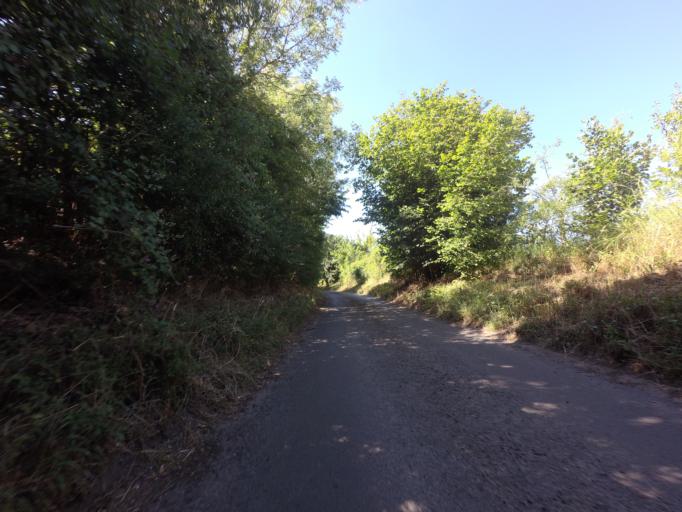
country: GB
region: England
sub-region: Kent
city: Dartford
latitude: 51.4069
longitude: 0.2105
